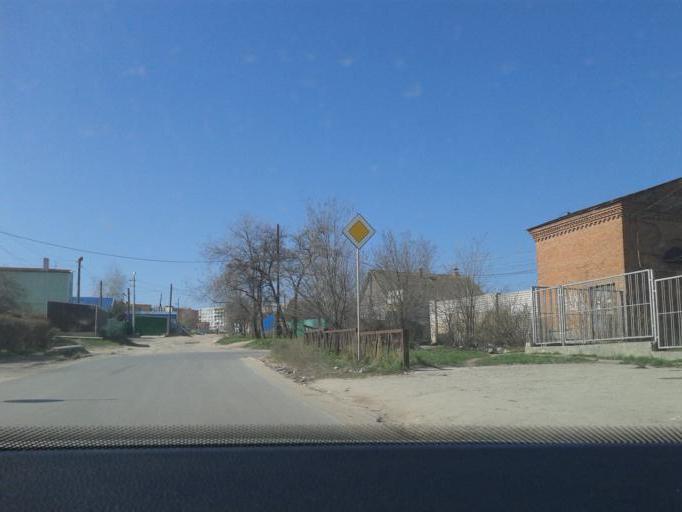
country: RU
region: Volgograd
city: Volgograd
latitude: 48.6817
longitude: 44.4569
